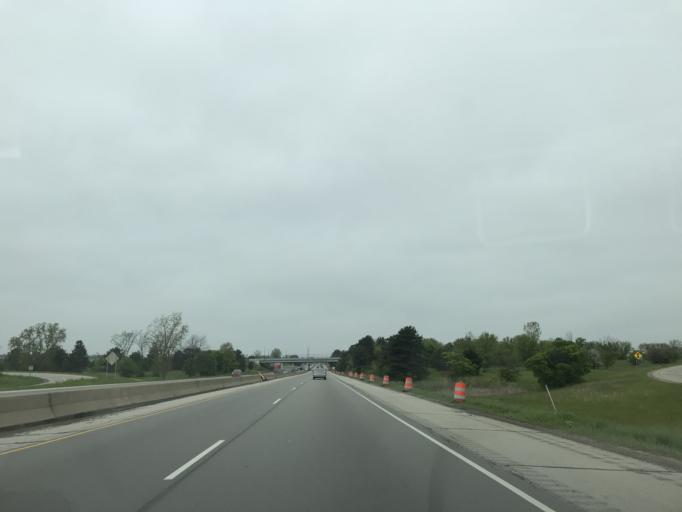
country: US
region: Michigan
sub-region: Washtenaw County
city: Ann Arbor
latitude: 42.2431
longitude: -83.7600
